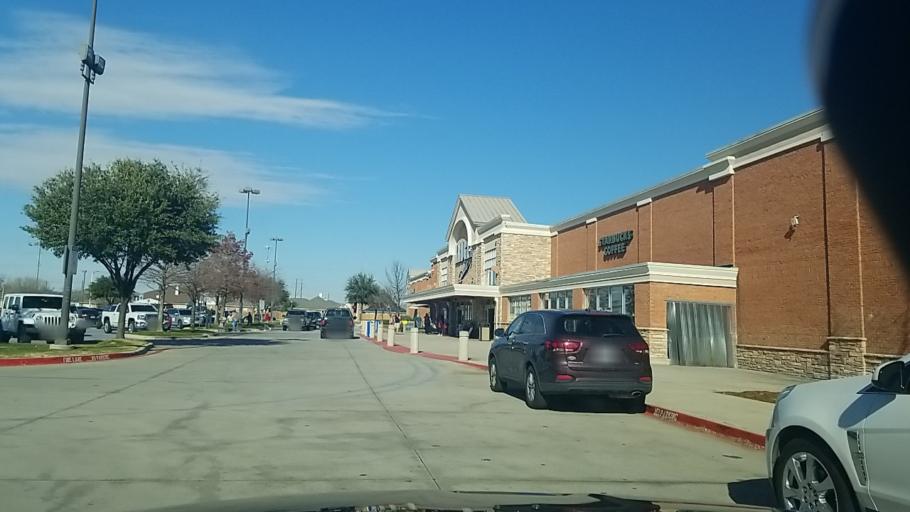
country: US
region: Texas
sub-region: Denton County
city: Corinth
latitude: 33.1452
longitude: -97.1024
